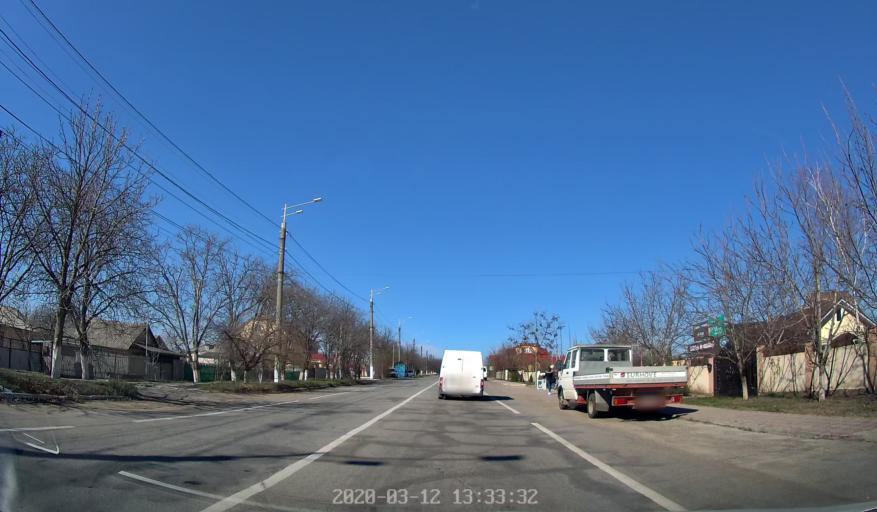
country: MD
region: Laloveni
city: Ialoveni
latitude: 46.9574
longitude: 28.7688
